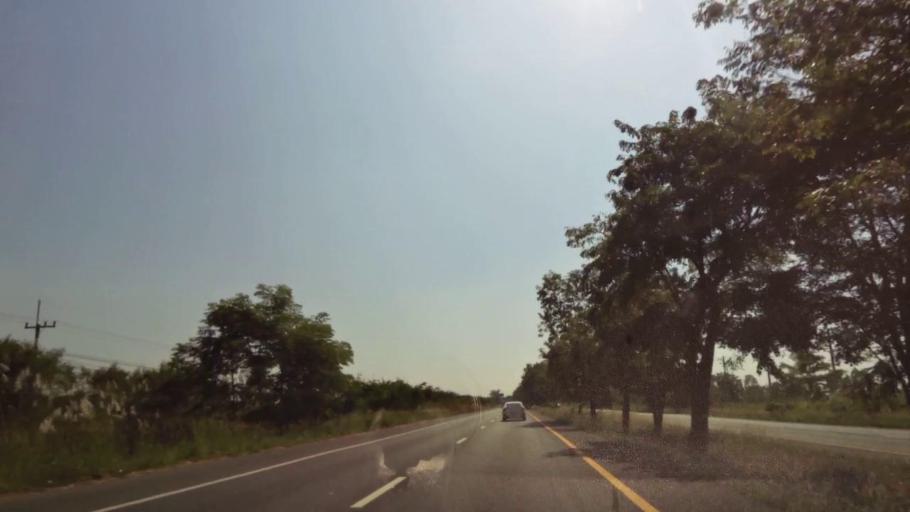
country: TH
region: Nakhon Sawan
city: Kao Liao
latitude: 15.9237
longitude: 100.1120
